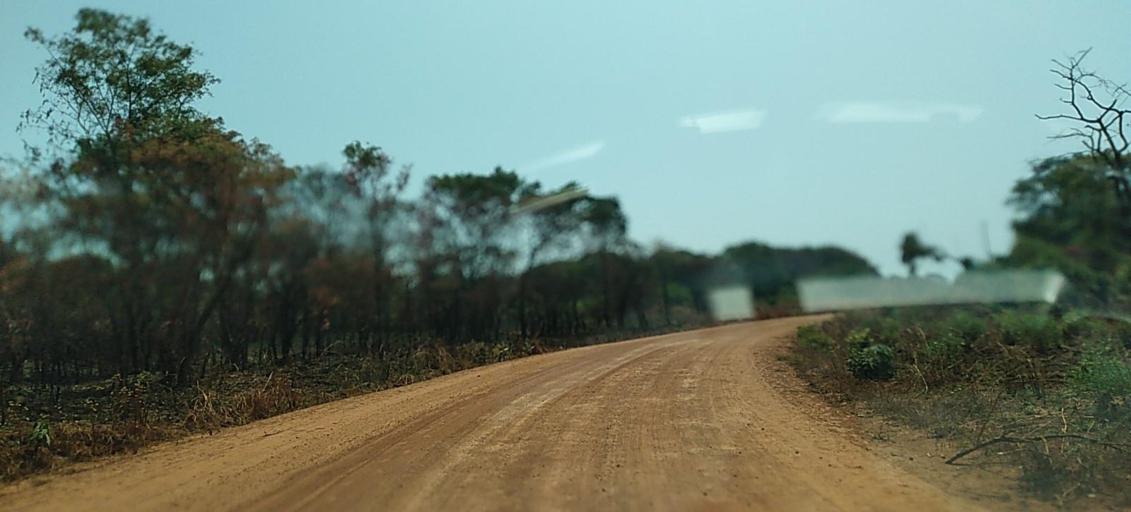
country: ZM
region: North-Western
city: Kansanshi
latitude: -11.9926
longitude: 26.6180
